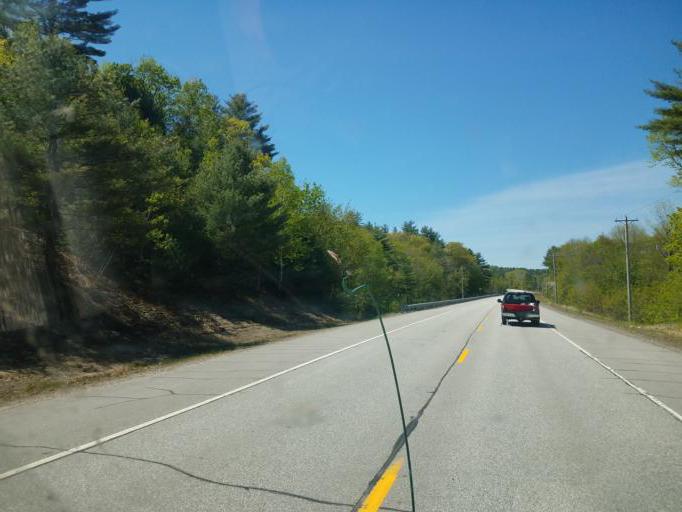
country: US
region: New Hampshire
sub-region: Grafton County
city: Rumney
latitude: 43.8100
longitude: -71.8647
